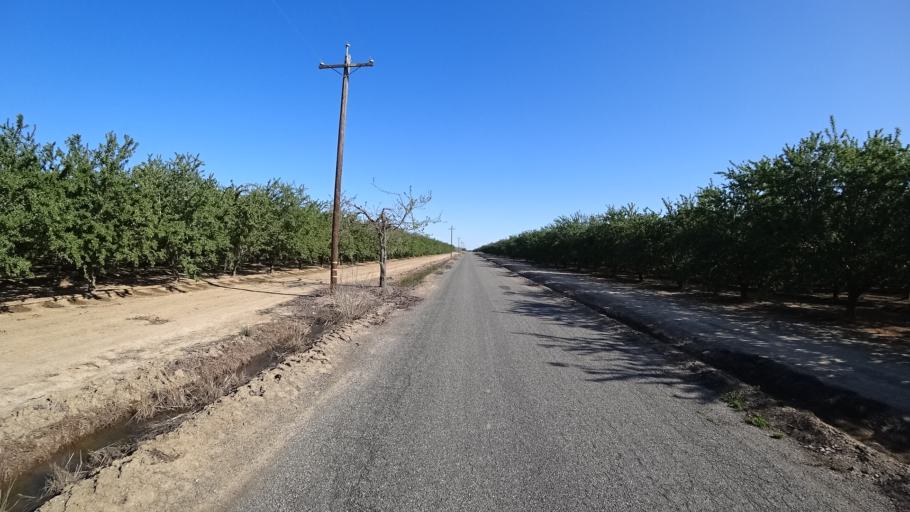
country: US
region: California
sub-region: Glenn County
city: Hamilton City
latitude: 39.6958
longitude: -122.0642
